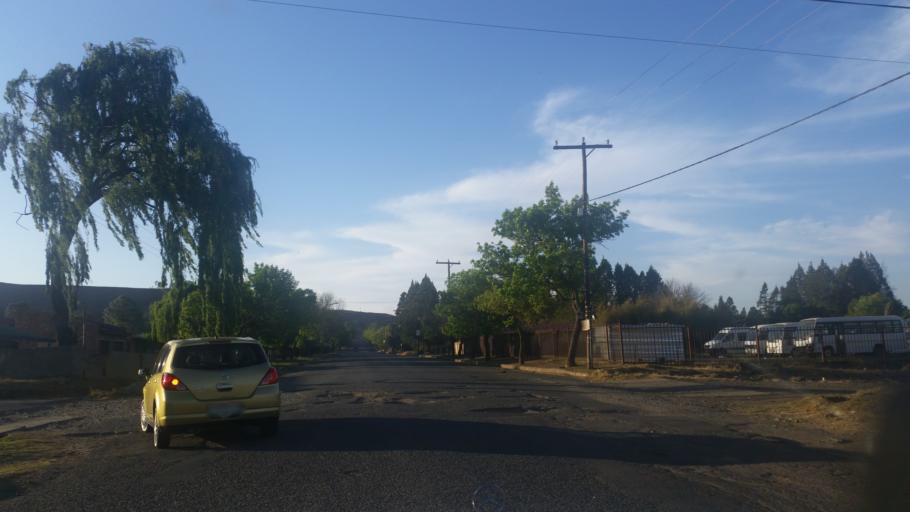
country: ZA
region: Orange Free State
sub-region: Thabo Mofutsanyana District Municipality
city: Phuthaditjhaba
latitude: -28.3175
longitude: 28.7050
